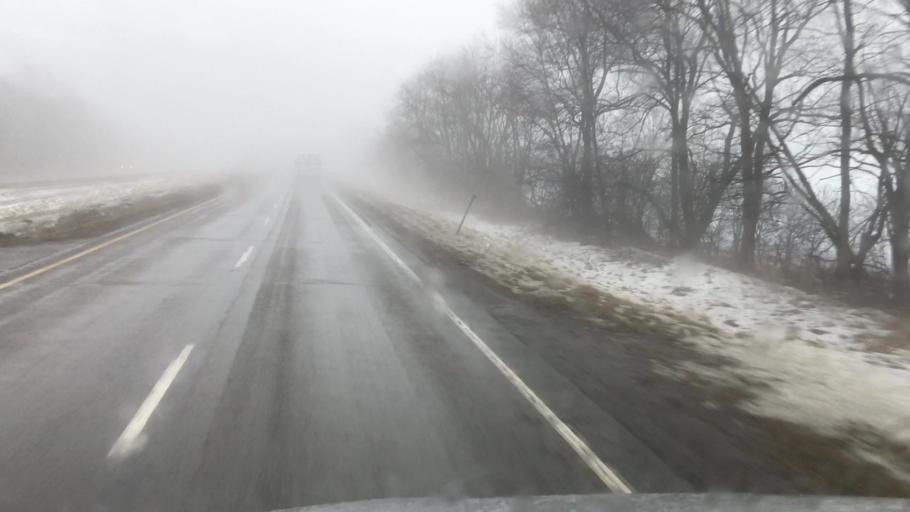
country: US
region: Indiana
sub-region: Newton County
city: Roselawn
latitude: 41.1291
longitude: -87.4532
